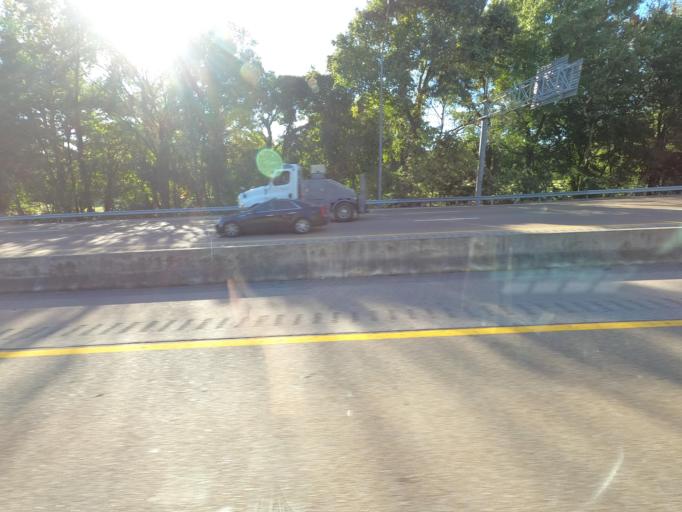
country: US
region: Tennessee
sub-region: Shelby County
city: New South Memphis
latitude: 35.0918
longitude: -90.0256
